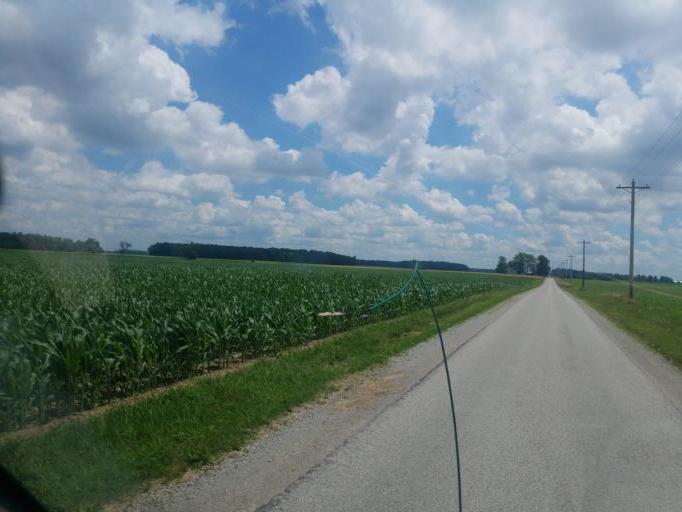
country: US
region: Ohio
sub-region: Huron County
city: Willard
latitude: 41.0283
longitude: -82.8307
